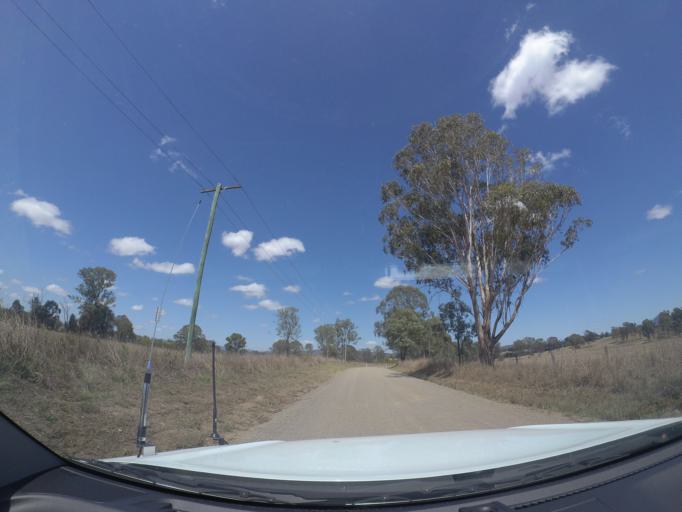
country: AU
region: Queensland
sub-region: Logan
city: North Maclean
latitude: -27.8384
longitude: 152.9221
